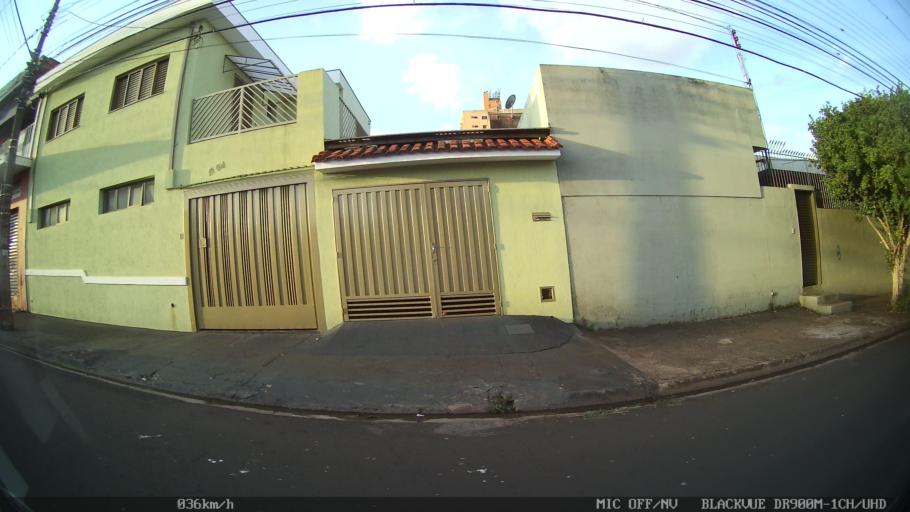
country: BR
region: Sao Paulo
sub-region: Ribeirao Preto
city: Ribeirao Preto
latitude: -21.1589
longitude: -47.8356
